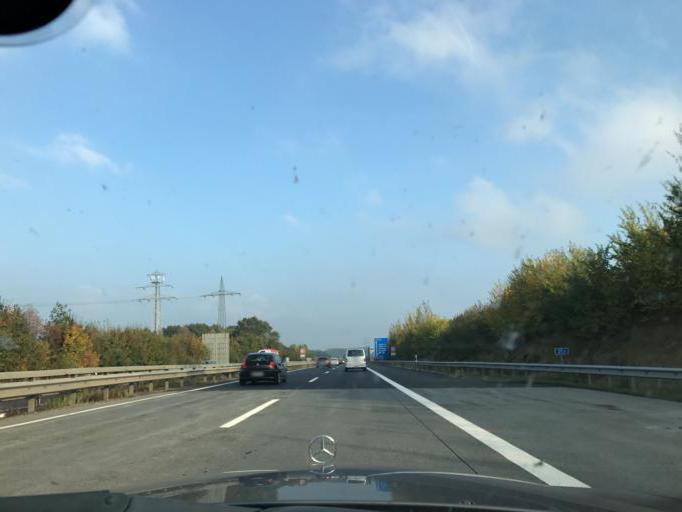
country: DE
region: Lower Saxony
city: Buchholz in der Nordheide
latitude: 53.3727
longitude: 9.8681
